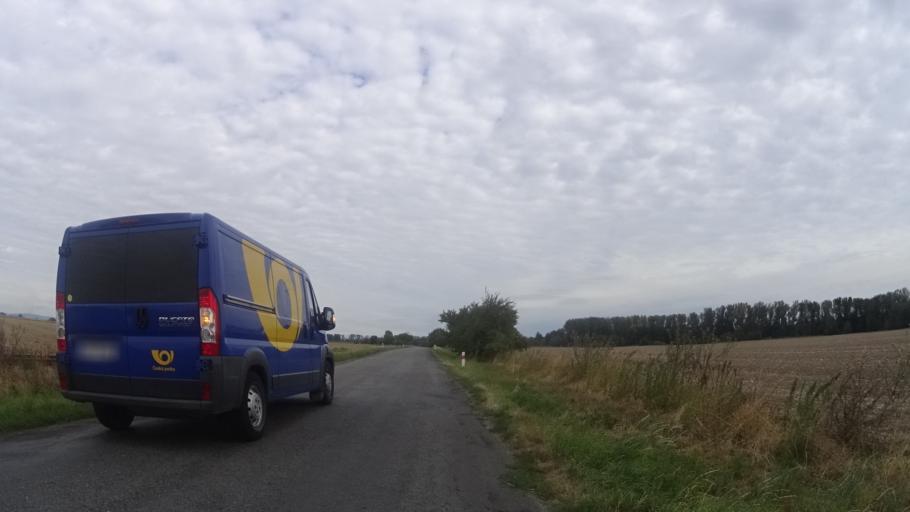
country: CZ
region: Olomoucky
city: Tovacov
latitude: 49.4105
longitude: 17.2835
